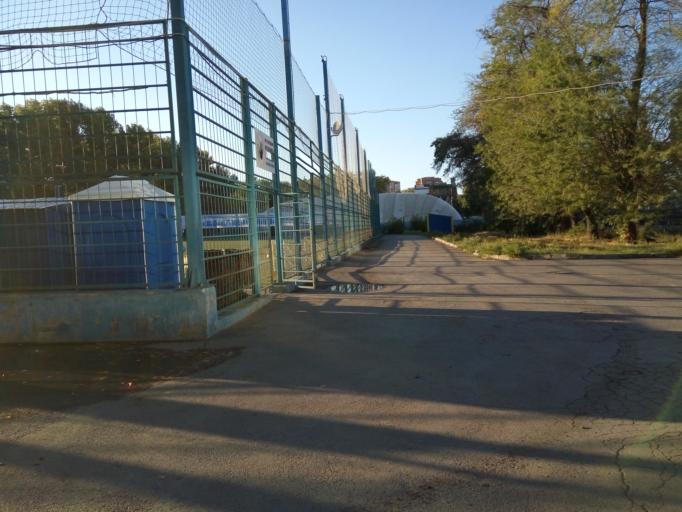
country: RU
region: Rostov
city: Rostov-na-Donu
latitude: 47.2439
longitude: 39.7587
